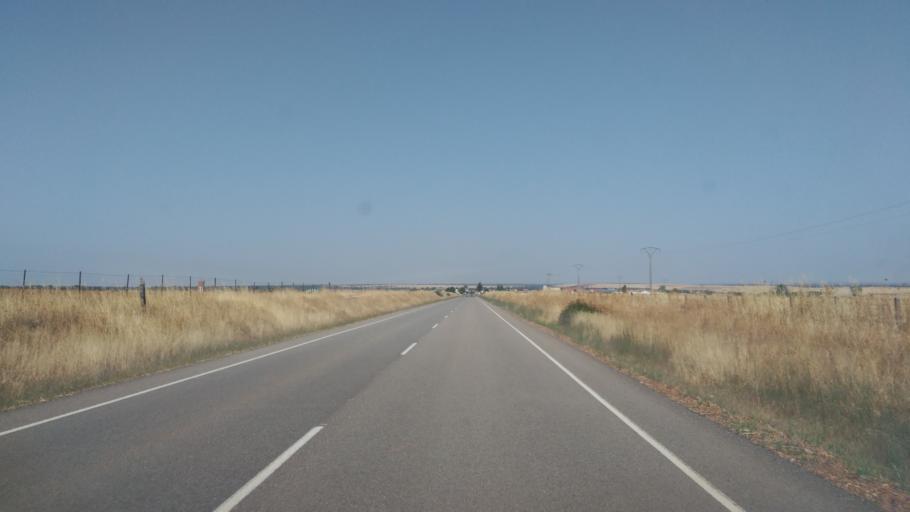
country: ES
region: Castille and Leon
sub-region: Provincia de Salamanca
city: Abusejo
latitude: 40.7008
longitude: -6.1364
